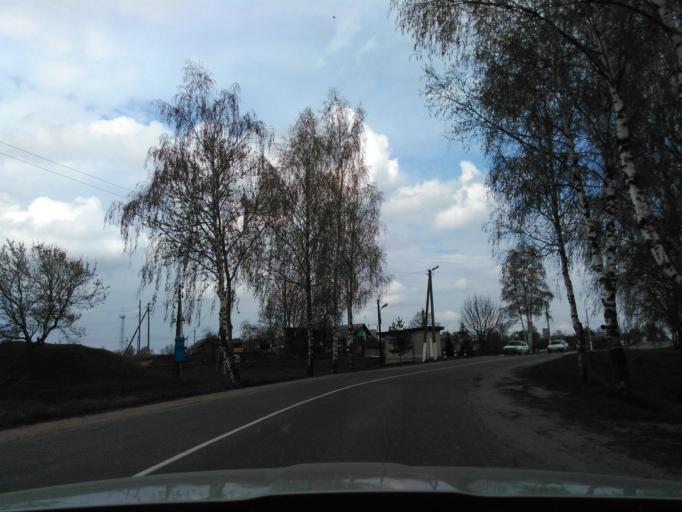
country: BY
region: Vitebsk
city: Chashniki
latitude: 54.8406
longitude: 29.1786
